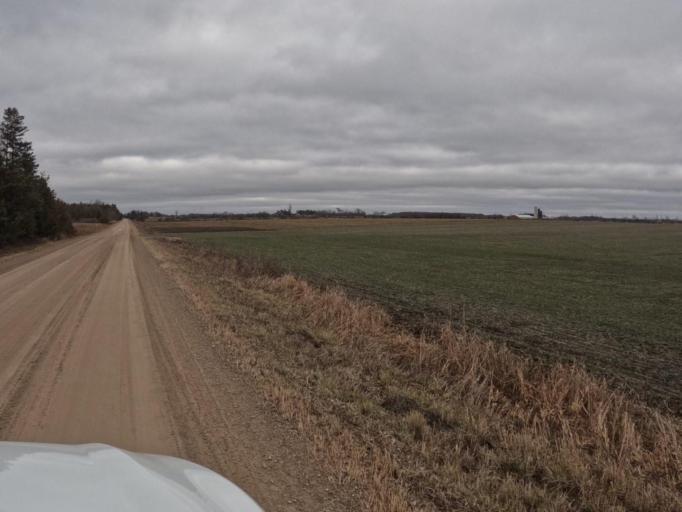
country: CA
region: Ontario
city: Shelburne
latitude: 43.9478
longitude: -80.3961
